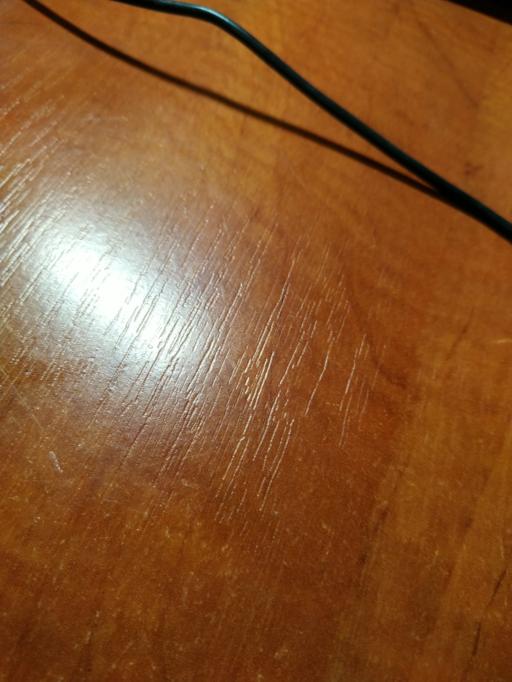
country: RU
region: Novgorod
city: Uglovka
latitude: 58.2963
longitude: 33.5918
